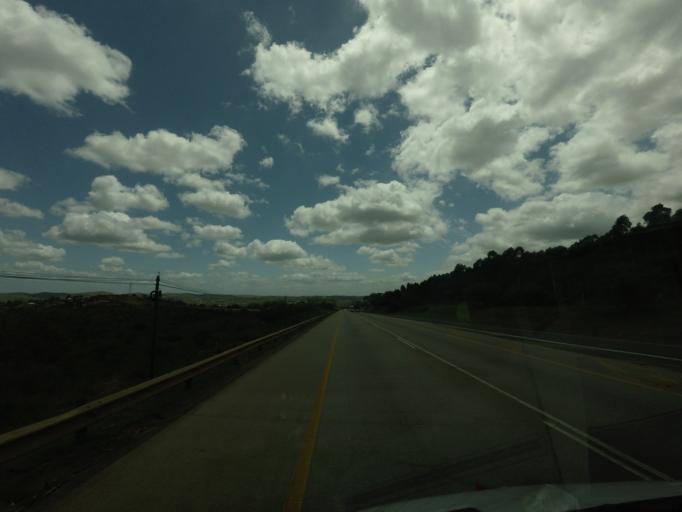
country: ZA
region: KwaZulu-Natal
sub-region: uMkhanyakude District Municipality
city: Mtubatuba
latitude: -28.4665
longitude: 32.1471
